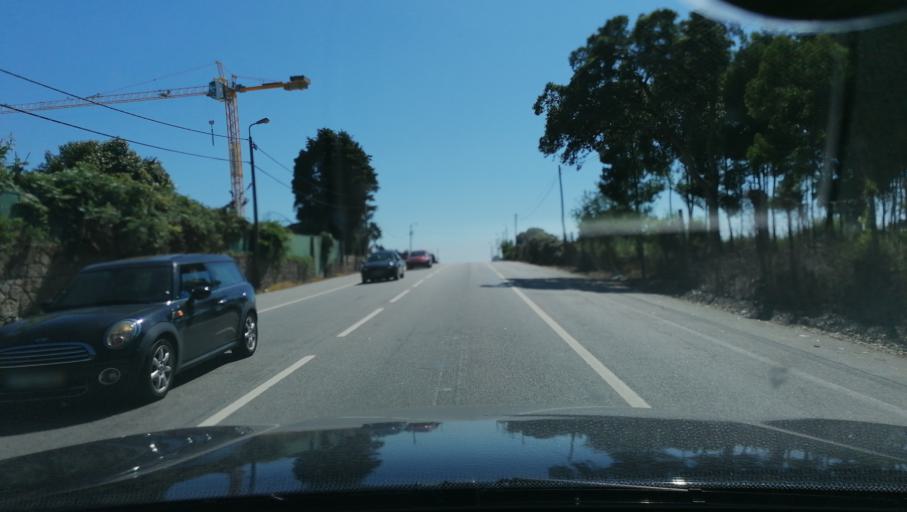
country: PT
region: Porto
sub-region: Vila Nova de Gaia
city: Vila Nova da Telha
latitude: 41.0801
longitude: -8.6367
